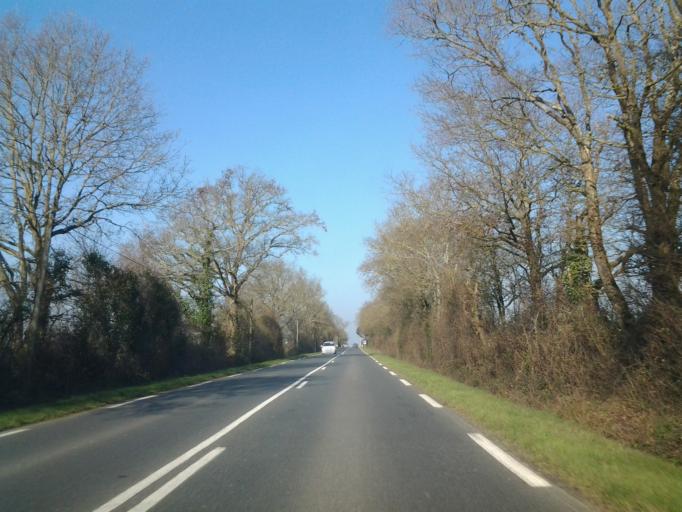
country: FR
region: Pays de la Loire
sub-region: Departement de la Vendee
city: Mache
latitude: 46.7844
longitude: -1.6943
